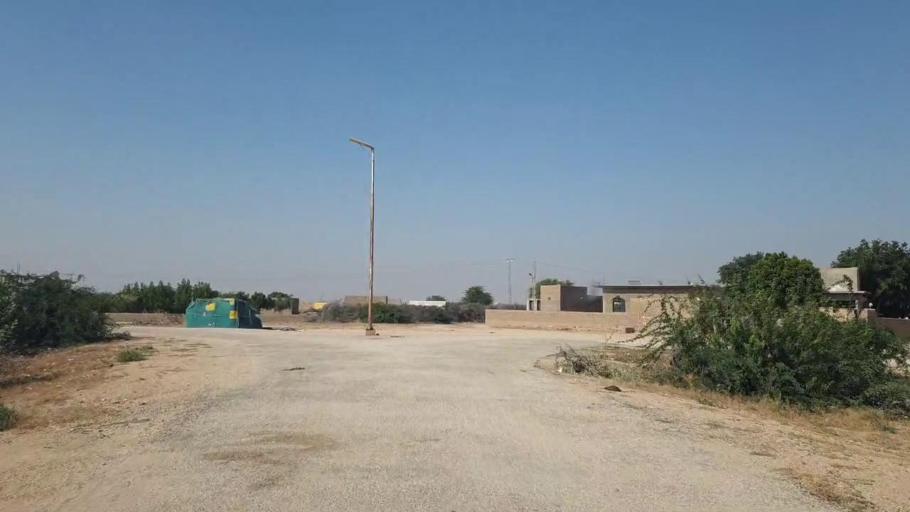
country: PK
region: Sindh
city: Jamshoro
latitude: 25.3521
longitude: 67.8313
